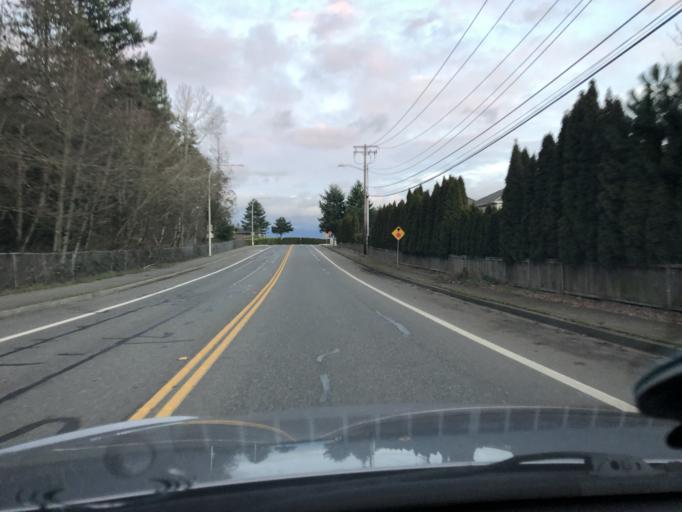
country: US
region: Washington
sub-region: King County
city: Lakeland North
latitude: 47.3188
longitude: -122.2622
